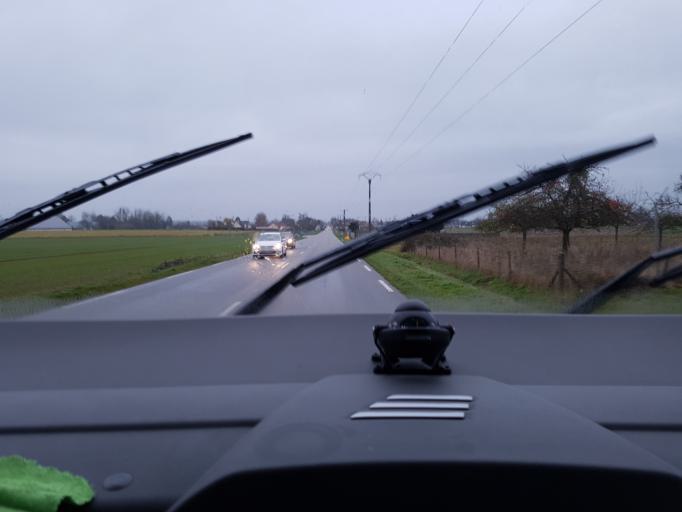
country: FR
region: Haute-Normandie
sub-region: Departement de l'Eure
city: Le Neubourg
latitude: 49.1298
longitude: 0.8755
